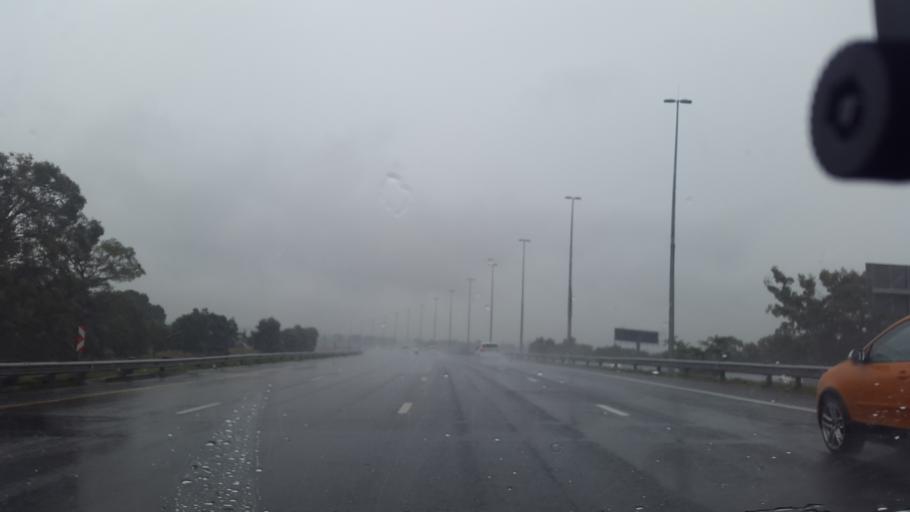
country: ZA
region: Gauteng
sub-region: City of Johannesburg Metropolitan Municipality
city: Johannesburg
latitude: -26.2280
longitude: 27.9613
